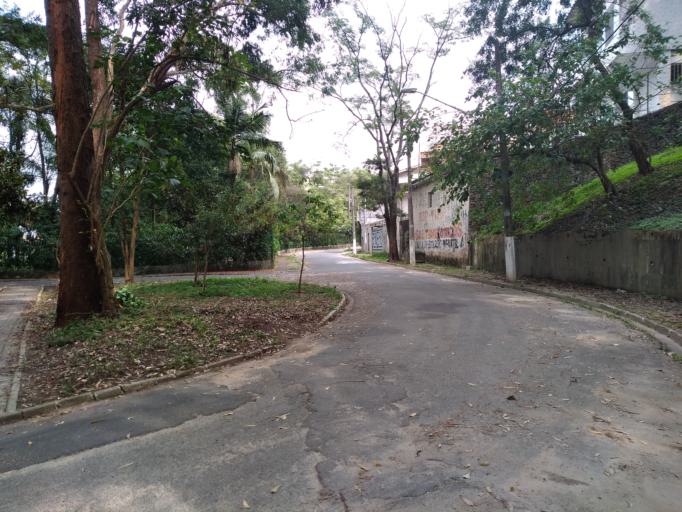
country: BR
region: Sao Paulo
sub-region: Taboao Da Serra
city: Taboao da Serra
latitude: -23.5820
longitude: -46.7305
